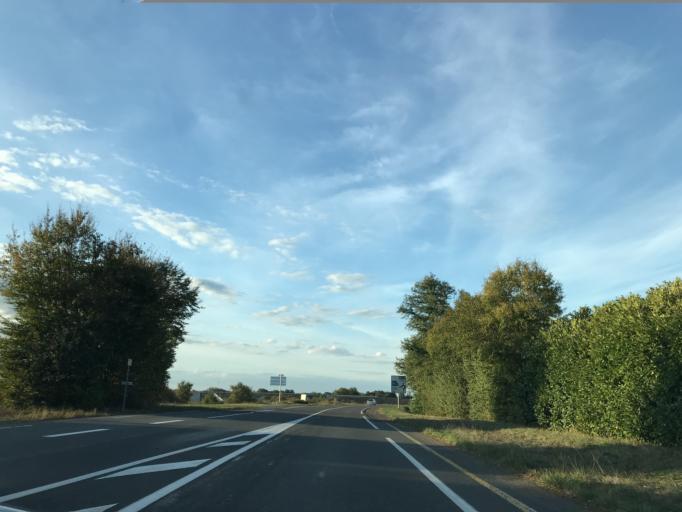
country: FR
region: Auvergne
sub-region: Departement de l'Allier
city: Saint-Yorre
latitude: 46.0422
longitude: 3.4734
